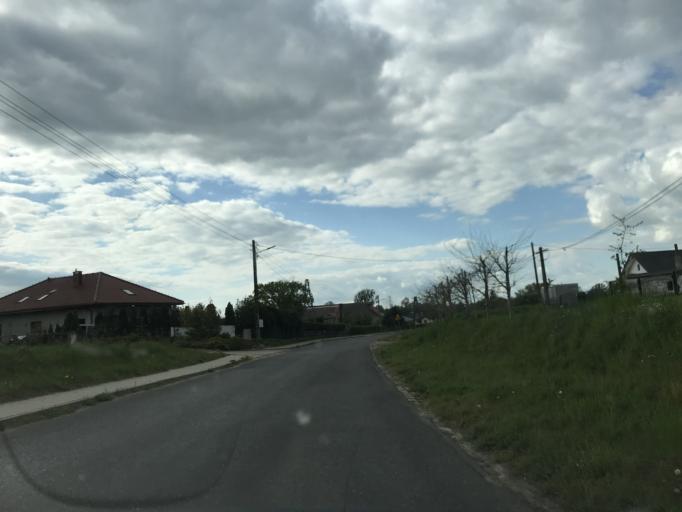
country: PL
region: West Pomeranian Voivodeship
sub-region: Powiat mysliborski
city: Mysliborz
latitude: 52.9172
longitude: 14.8870
